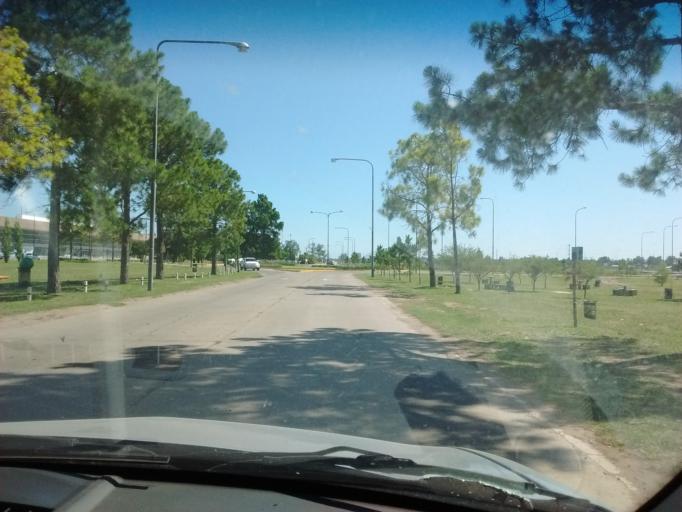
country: AR
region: Santa Fe
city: Funes
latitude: -32.9189
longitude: -60.7801
